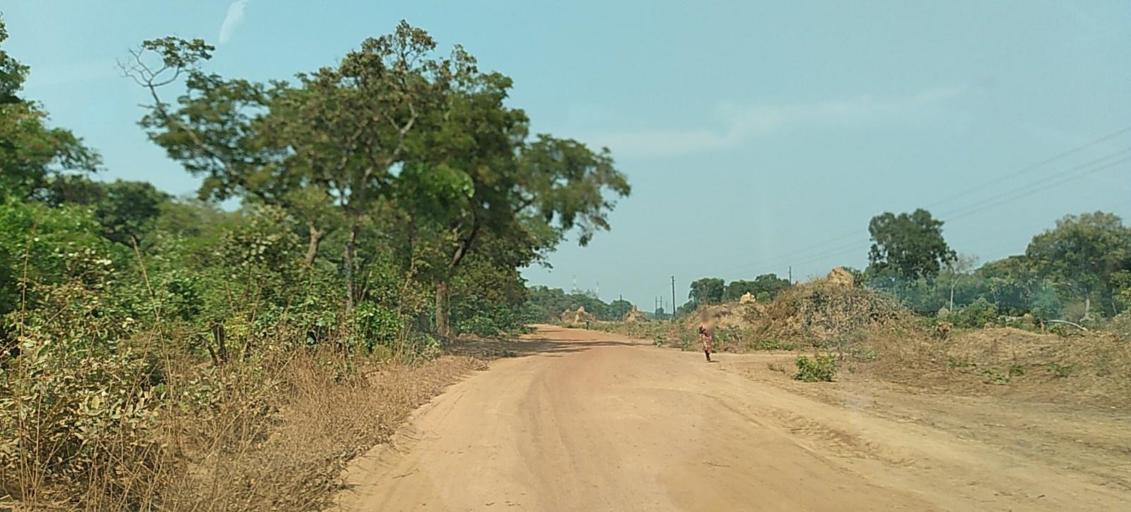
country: ZM
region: Copperbelt
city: Chingola
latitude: -13.0422
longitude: 27.4427
